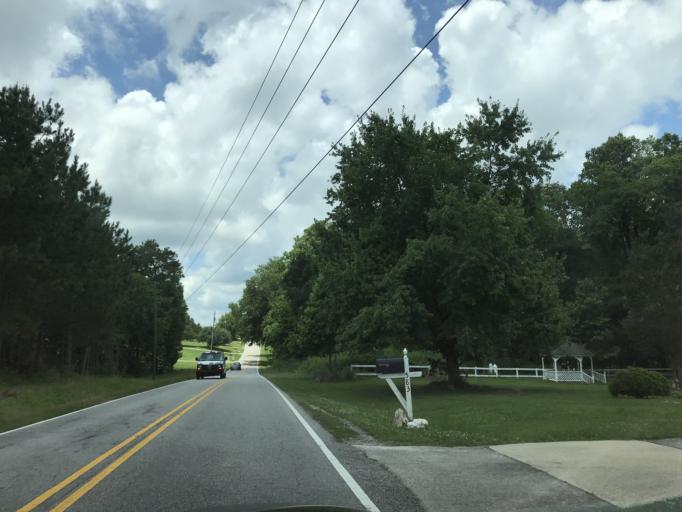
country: US
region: North Carolina
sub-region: Wake County
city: Rolesville
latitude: 35.9528
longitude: -78.3887
